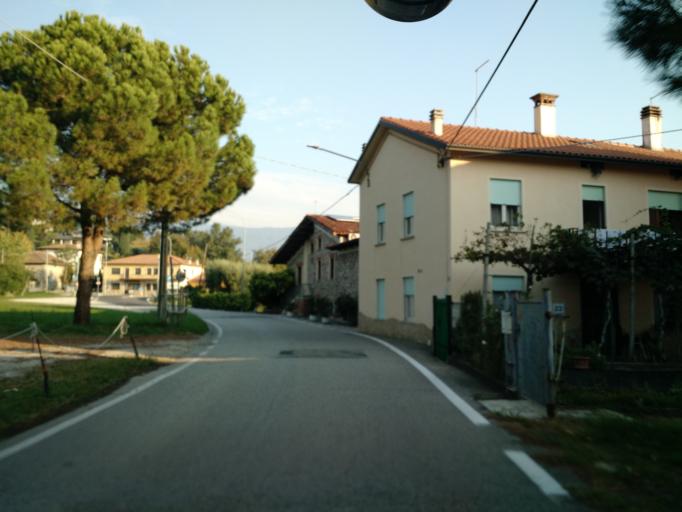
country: IT
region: Veneto
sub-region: Provincia di Vicenza
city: Sarcedo
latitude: 45.7020
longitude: 11.5384
